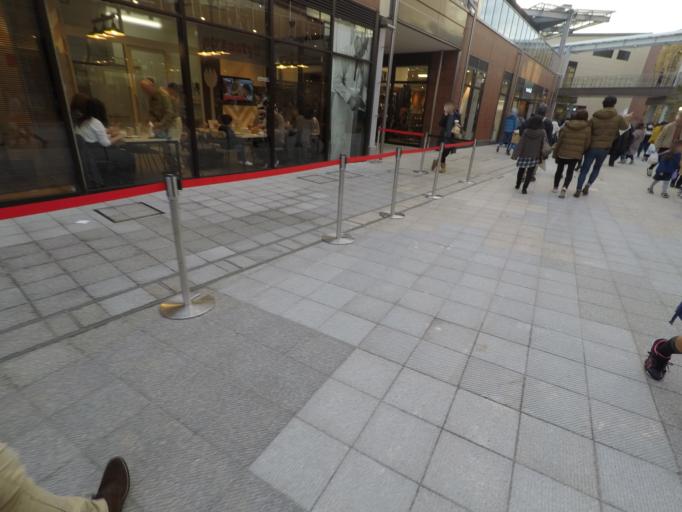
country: JP
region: Kanagawa
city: Minami-rinkan
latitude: 35.5086
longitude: 139.4713
